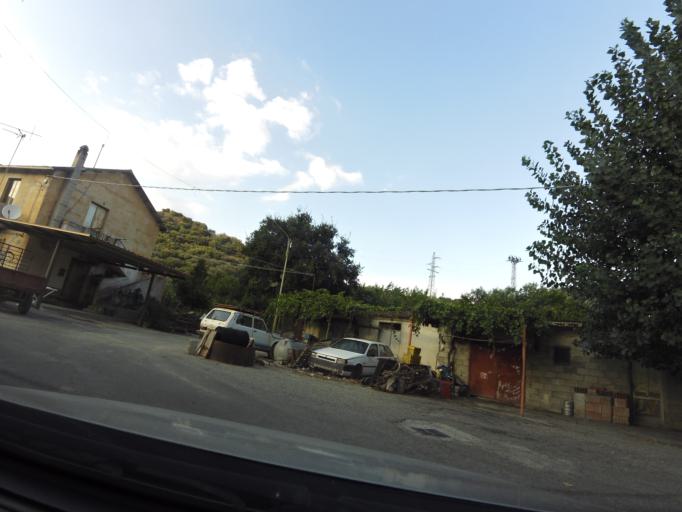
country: IT
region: Calabria
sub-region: Provincia di Reggio Calabria
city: Stilo
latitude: 38.4669
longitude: 16.4938
